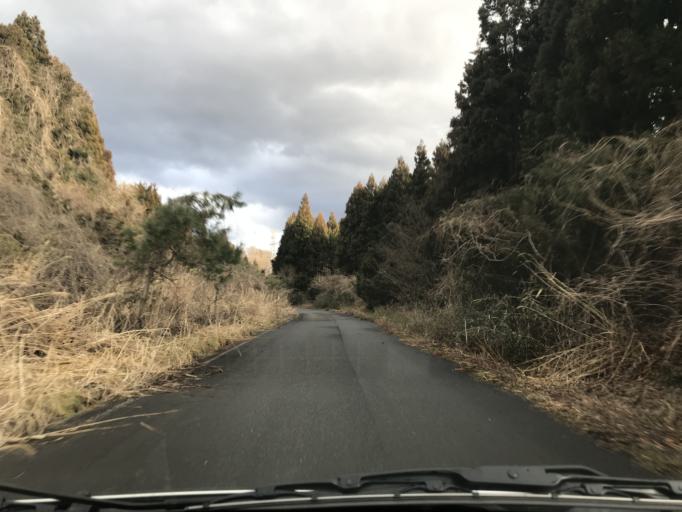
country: JP
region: Iwate
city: Mizusawa
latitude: 39.0324
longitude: 141.0813
